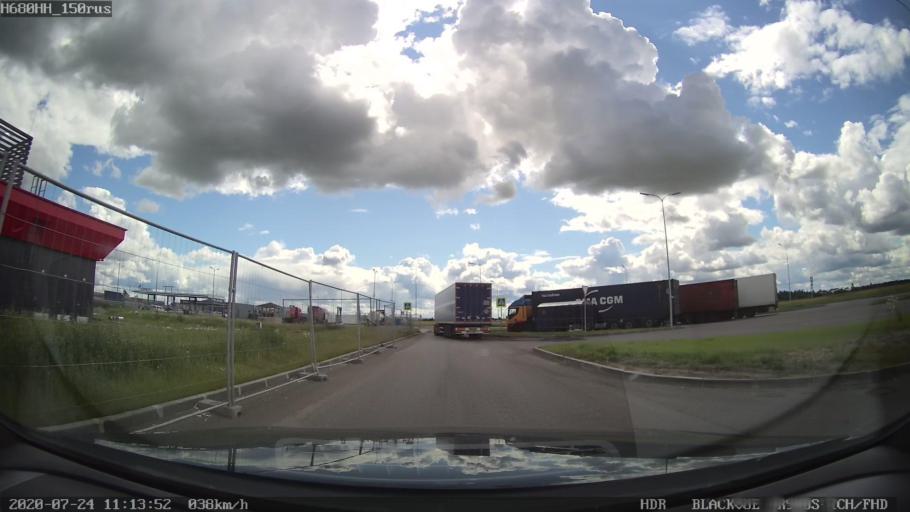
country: RU
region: Leningrad
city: Fedorovskoye
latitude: 59.7013
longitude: 30.5507
